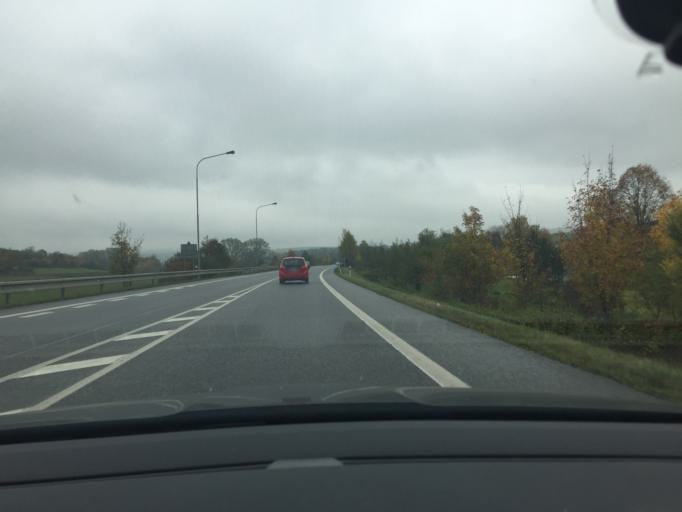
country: CZ
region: Zlin
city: Popovice
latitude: 49.0437
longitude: 17.5291
